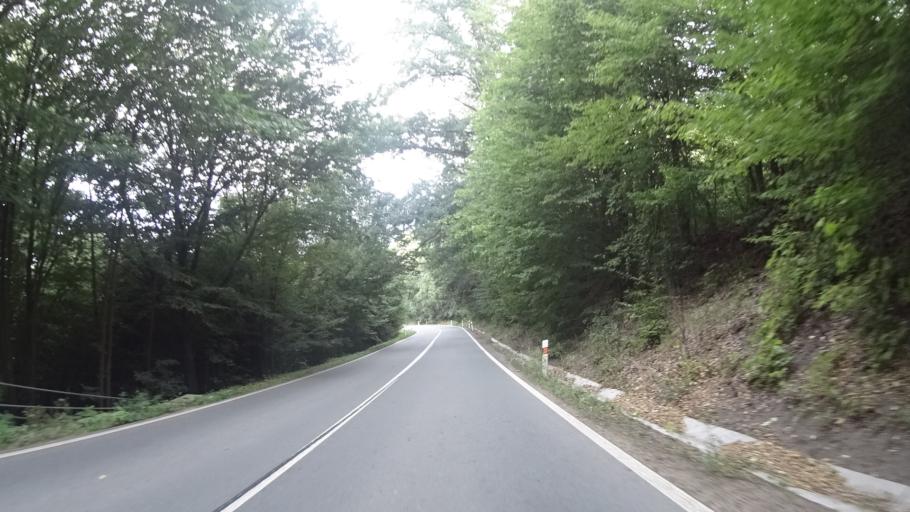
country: CZ
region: Pardubicky
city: Kuncina
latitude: 49.8617
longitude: 16.7078
